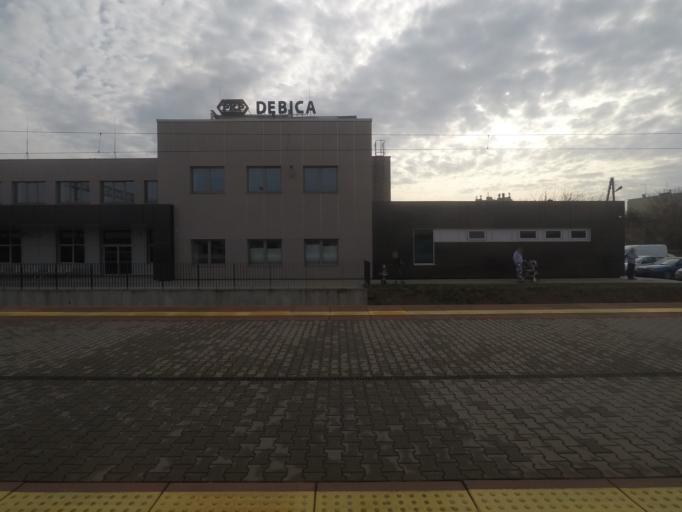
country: PL
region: Subcarpathian Voivodeship
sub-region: Powiat debicki
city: Debica
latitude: 50.0540
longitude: 21.4047
